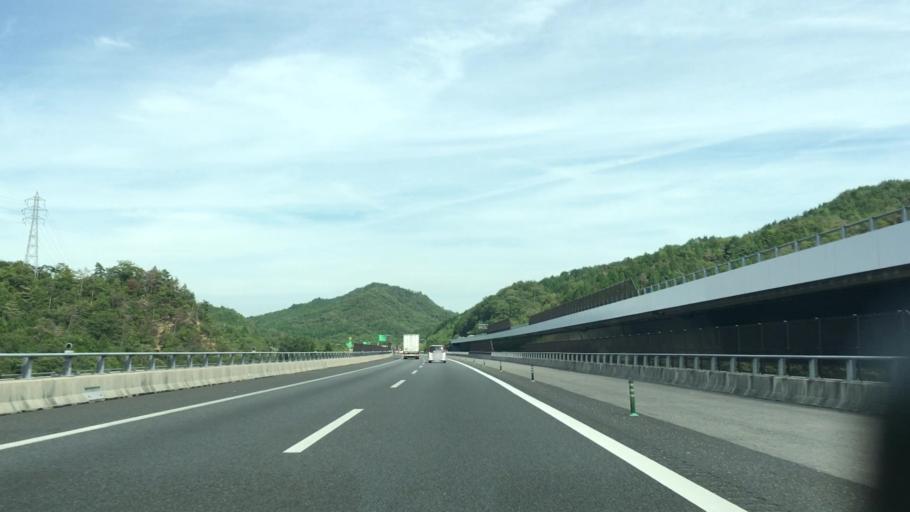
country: JP
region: Shiga Prefecture
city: Minakuchicho-matoba
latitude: 34.9236
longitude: 136.0940
